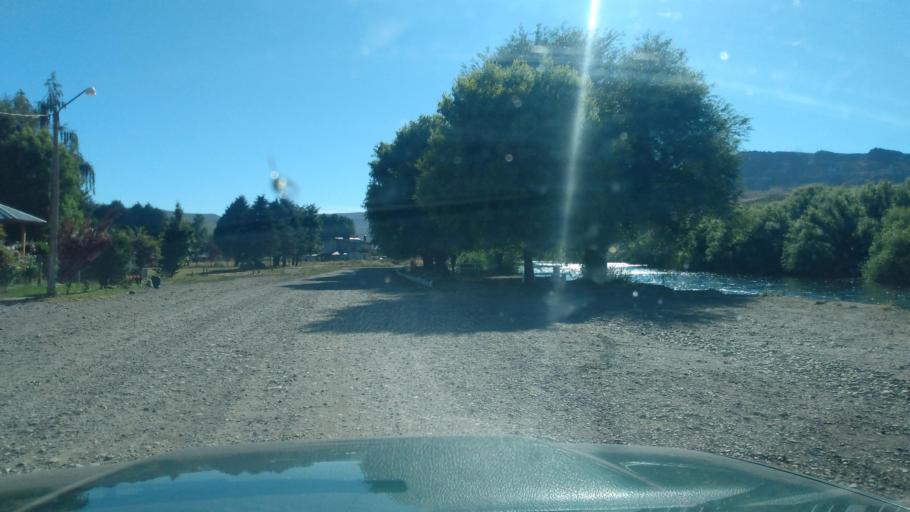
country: AR
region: Neuquen
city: Junin de los Andes
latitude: -39.9586
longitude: -71.0759
